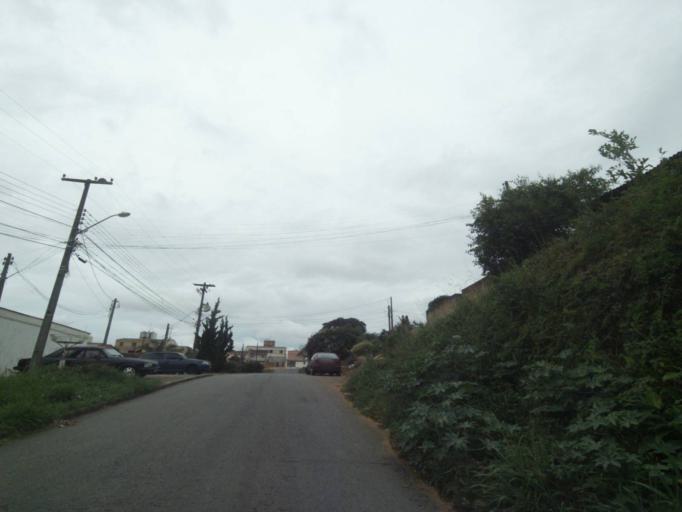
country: BR
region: Parana
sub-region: Curitiba
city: Curitiba
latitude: -25.4564
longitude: -49.3237
